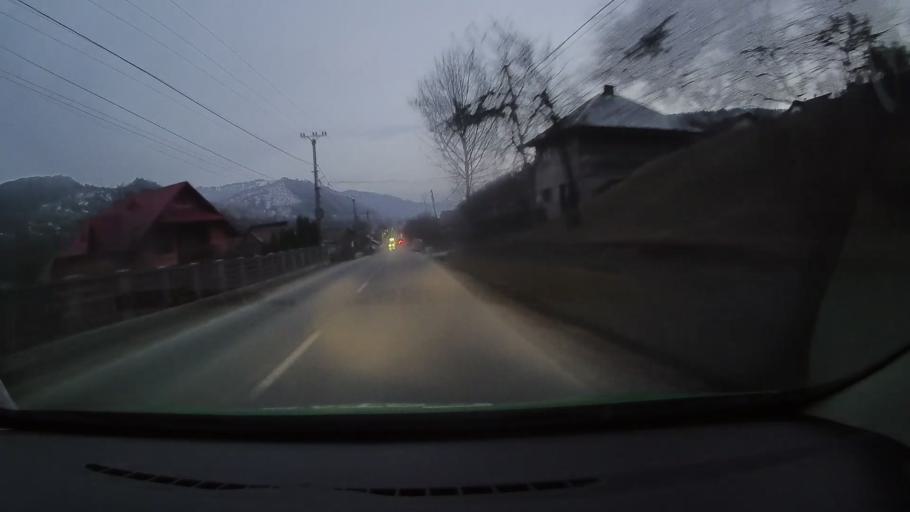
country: RO
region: Prahova
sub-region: Comuna Valea Doftanei
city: Tesila
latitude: 45.2959
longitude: 25.7204
